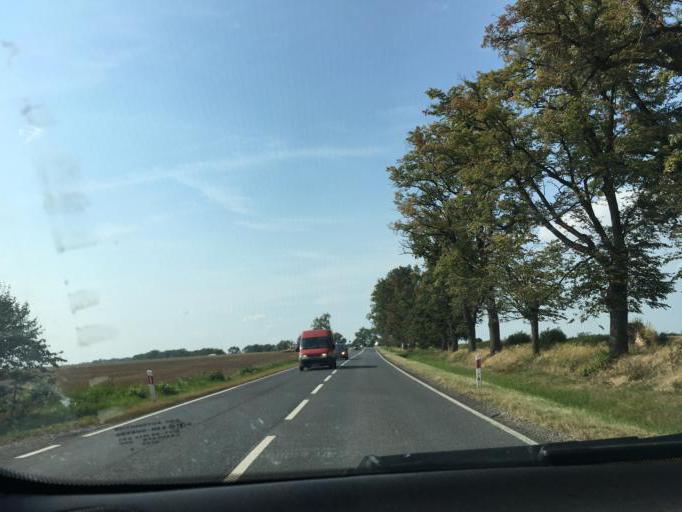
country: PL
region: Opole Voivodeship
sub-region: Powiat prudnicki
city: Laka Prudnicka
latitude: 50.4165
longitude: 17.4865
